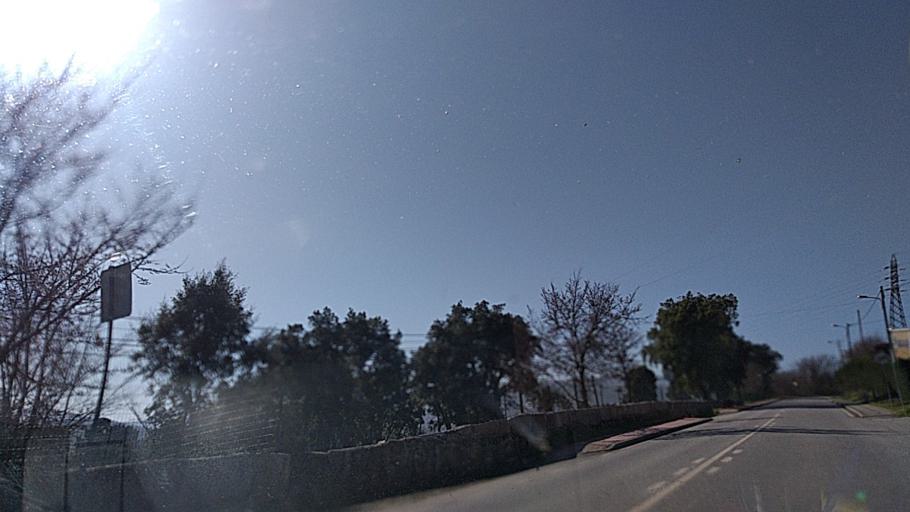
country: PT
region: Guarda
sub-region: Celorico da Beira
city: Celorico da Beira
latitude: 40.6476
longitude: -7.3833
